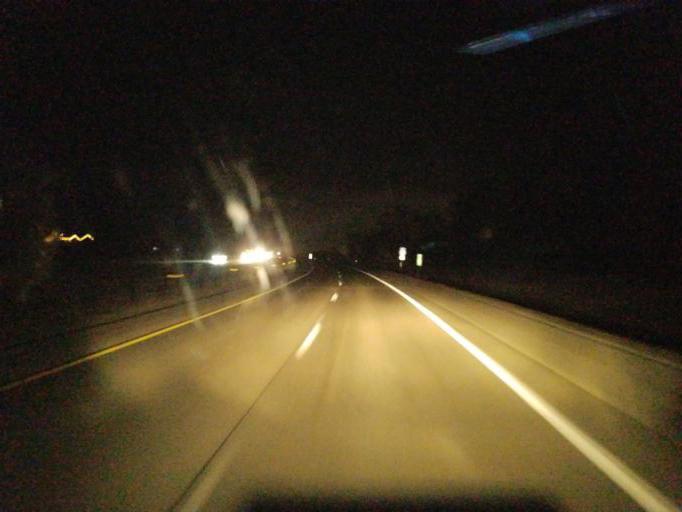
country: US
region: Iowa
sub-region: Dallas County
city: De Soto
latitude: 41.5213
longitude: -94.0676
